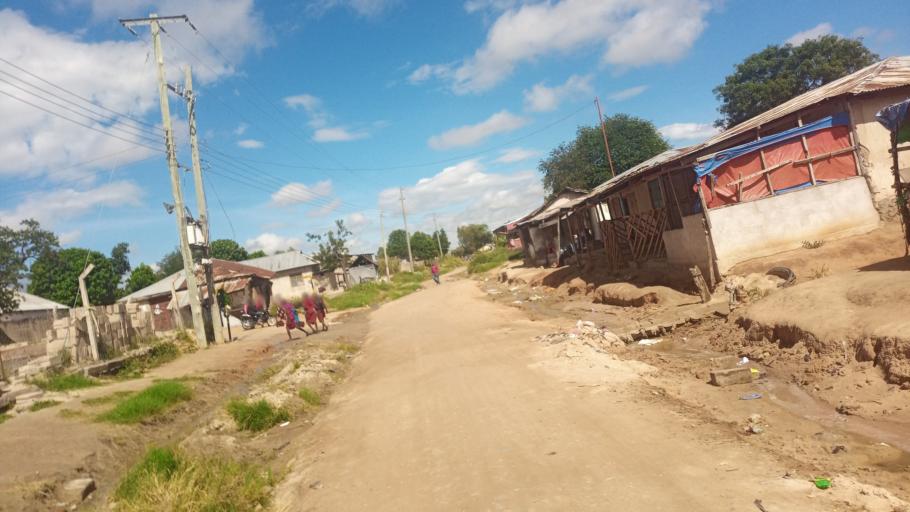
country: TZ
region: Dodoma
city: Dodoma
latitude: -6.1884
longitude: 35.7277
